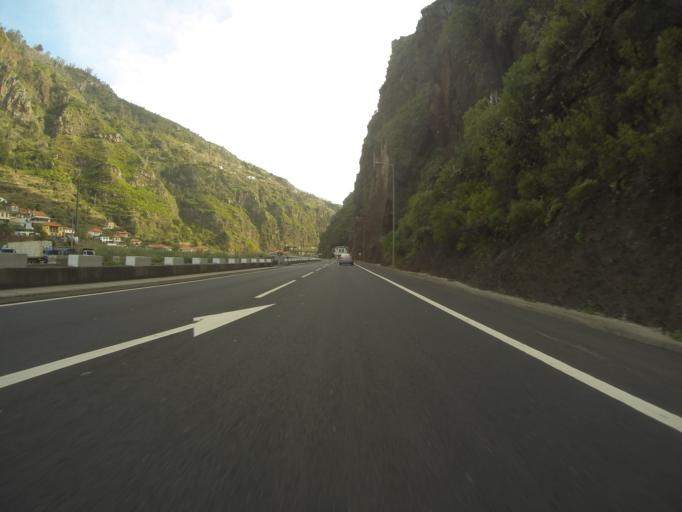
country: PT
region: Madeira
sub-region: Ribeira Brava
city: Campanario
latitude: 32.6895
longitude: -17.0505
